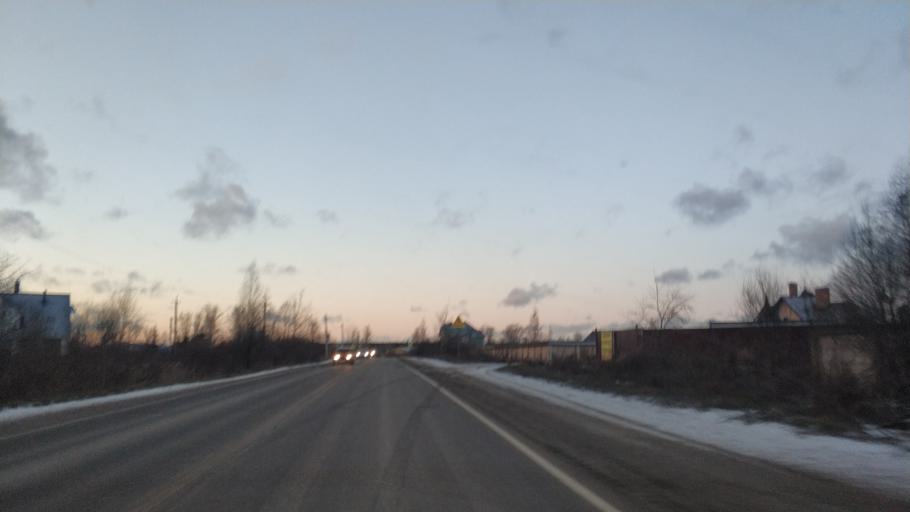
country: RU
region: St.-Petersburg
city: Pontonnyy
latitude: 59.8107
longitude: 30.6110
